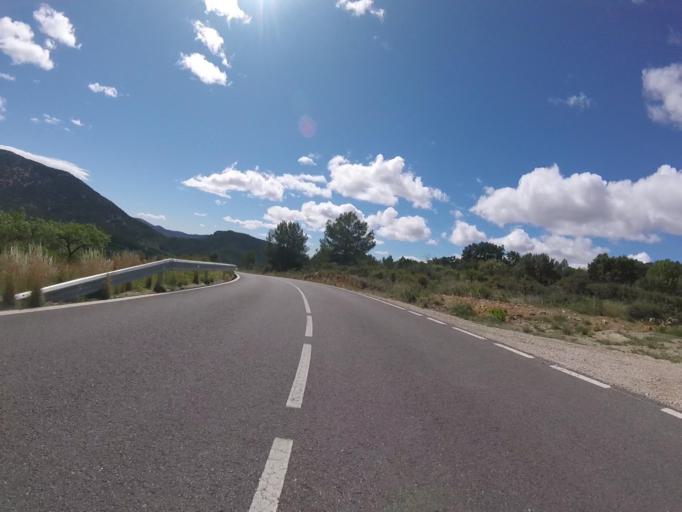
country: ES
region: Valencia
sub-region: Provincia de Castello
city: Culla
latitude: 40.2975
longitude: -0.1190
